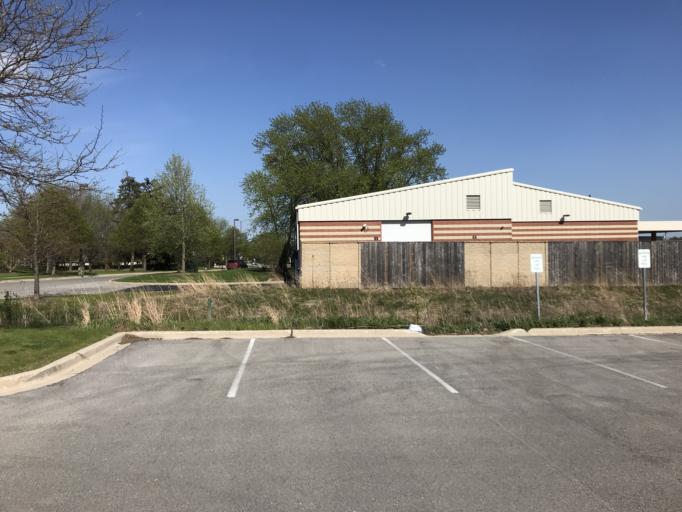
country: US
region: Illinois
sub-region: Will County
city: Plainfield
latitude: 41.7050
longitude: -88.1881
